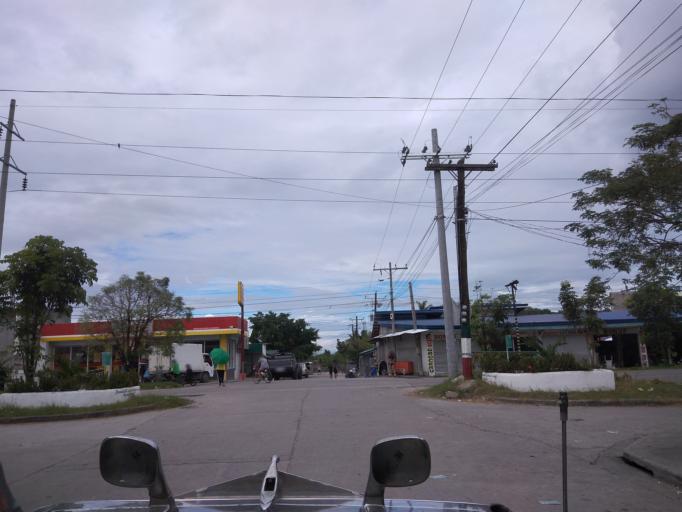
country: PH
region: Central Luzon
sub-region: Province of Pampanga
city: Pandacaqui
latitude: 15.1783
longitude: 120.6530
